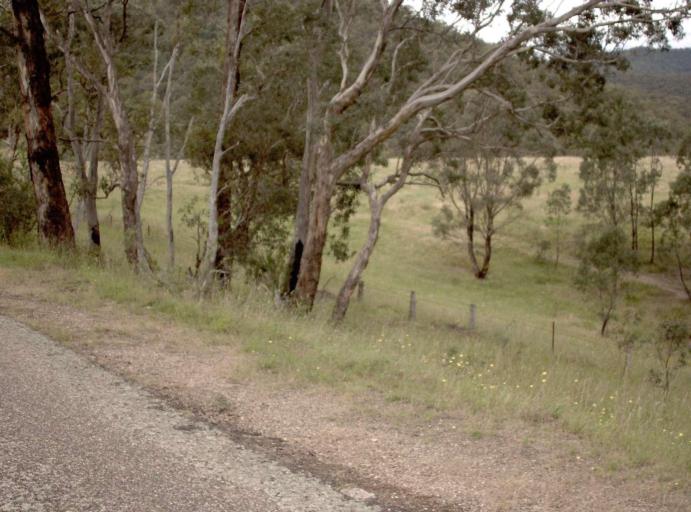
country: AU
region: Victoria
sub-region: East Gippsland
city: Bairnsdale
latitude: -37.5120
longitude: 147.2032
